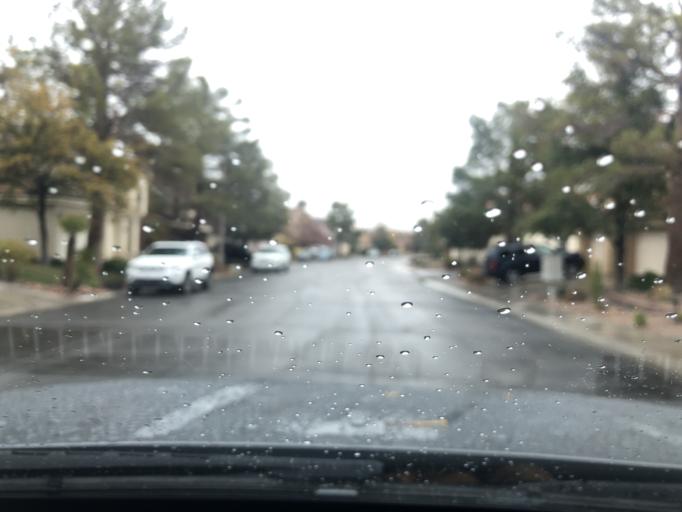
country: US
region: Nevada
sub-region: Clark County
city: Summerlin South
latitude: 36.1979
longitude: -115.2879
